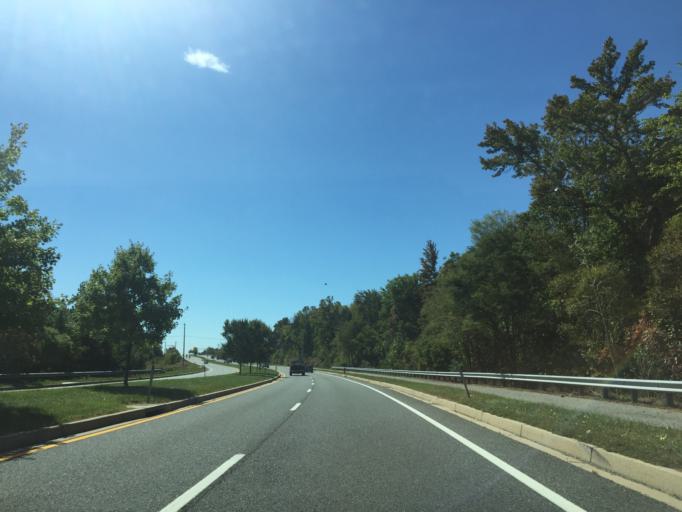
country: US
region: Maryland
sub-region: Baltimore County
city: Bowleys Quarters
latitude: 39.3456
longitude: -76.4144
